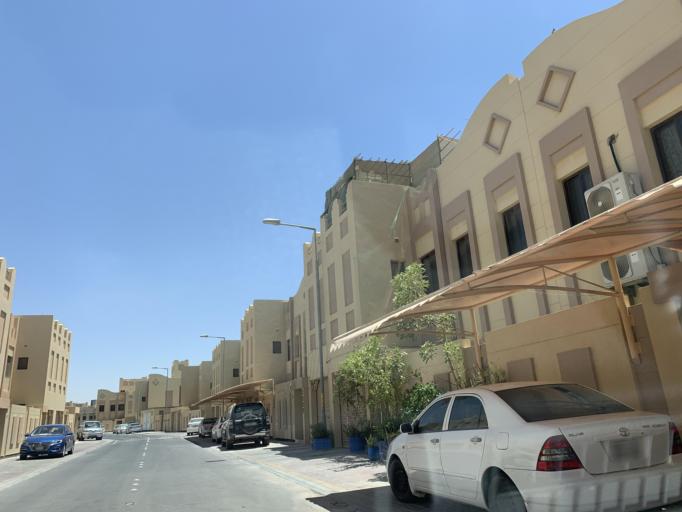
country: BH
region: Manama
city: Jidd Hafs
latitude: 26.2341
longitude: 50.4913
